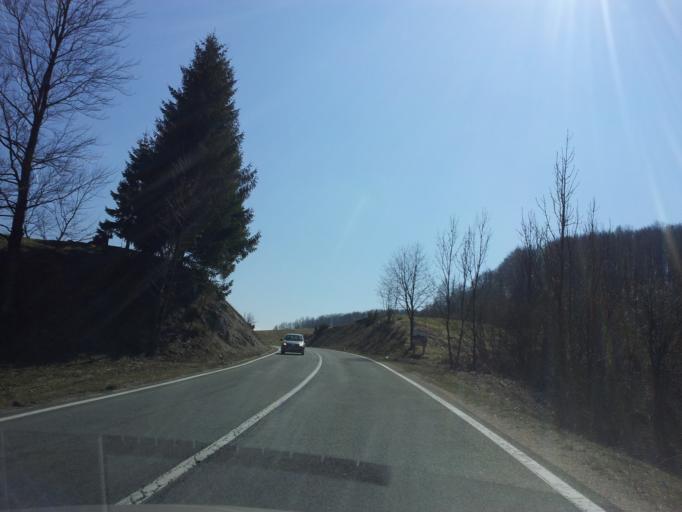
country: HR
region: Licko-Senjska
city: Jezerce
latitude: 44.8507
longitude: 15.6524
